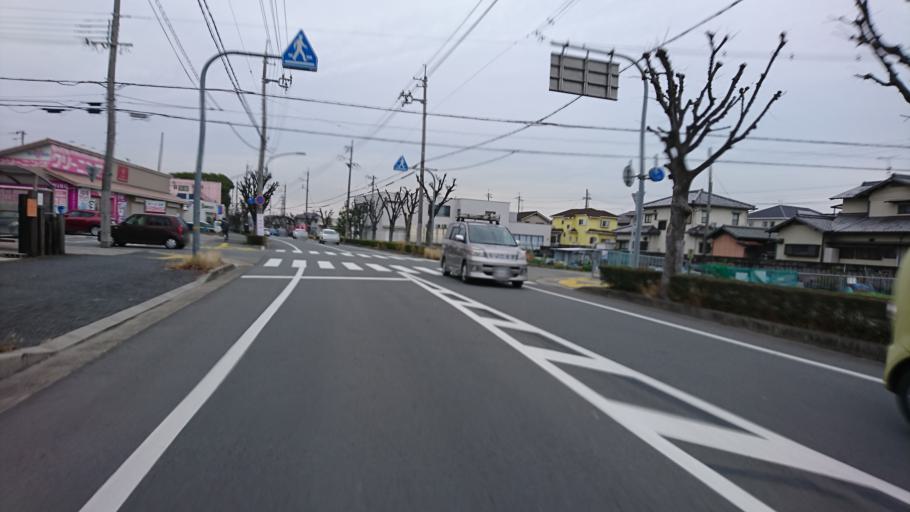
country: JP
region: Hyogo
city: Kakogawacho-honmachi
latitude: 34.7595
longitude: 134.8288
